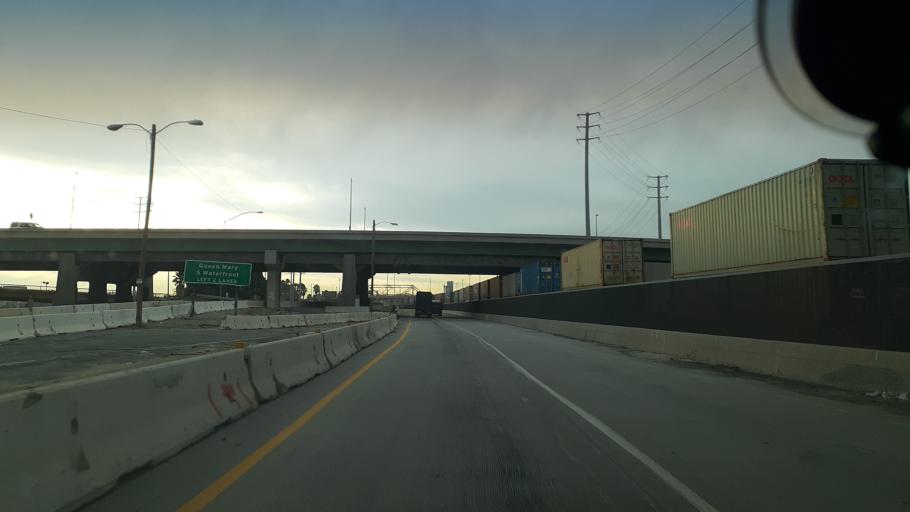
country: US
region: California
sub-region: Los Angeles County
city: Long Beach
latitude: 33.7680
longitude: -118.2076
